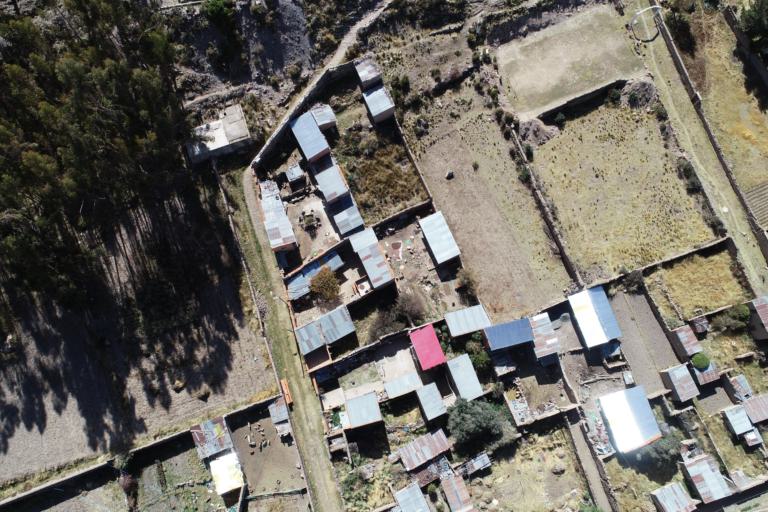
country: BO
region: La Paz
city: Achacachi
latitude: -15.8962
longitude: -68.9042
